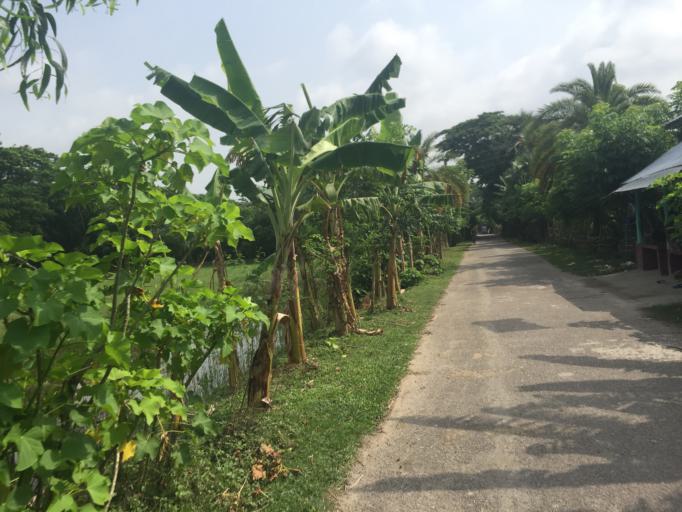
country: BD
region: Barisal
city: Mathba
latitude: 22.2590
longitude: 89.9112
